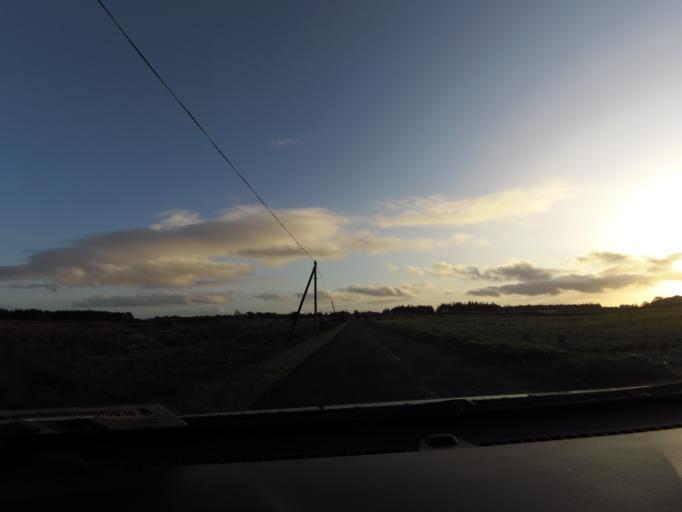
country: IE
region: Connaught
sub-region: Roscommon
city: Castlerea
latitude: 53.6473
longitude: -8.6062
